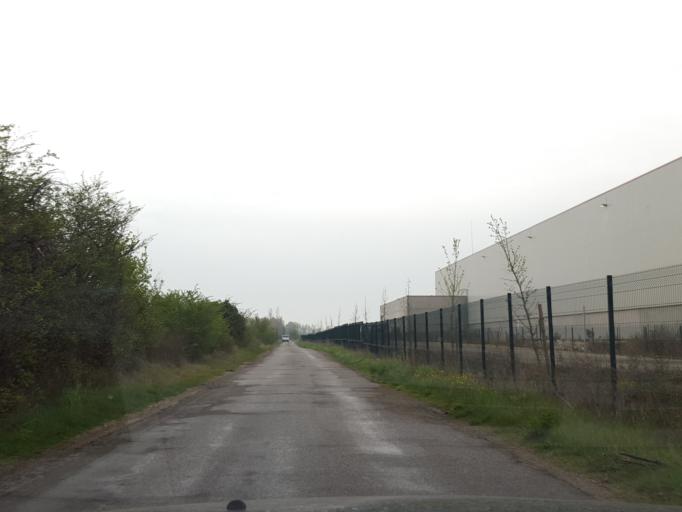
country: FR
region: Provence-Alpes-Cote d'Azur
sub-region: Departement du Vaucluse
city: Entraigues-sur-la-Sorgue
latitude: 43.9831
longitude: 4.9369
